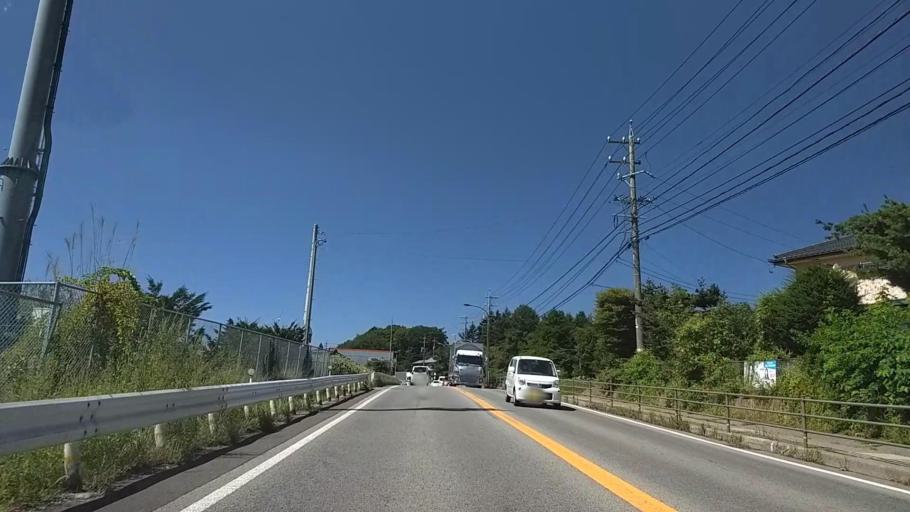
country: JP
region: Nagano
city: Komoro
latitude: 36.3434
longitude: 138.5600
